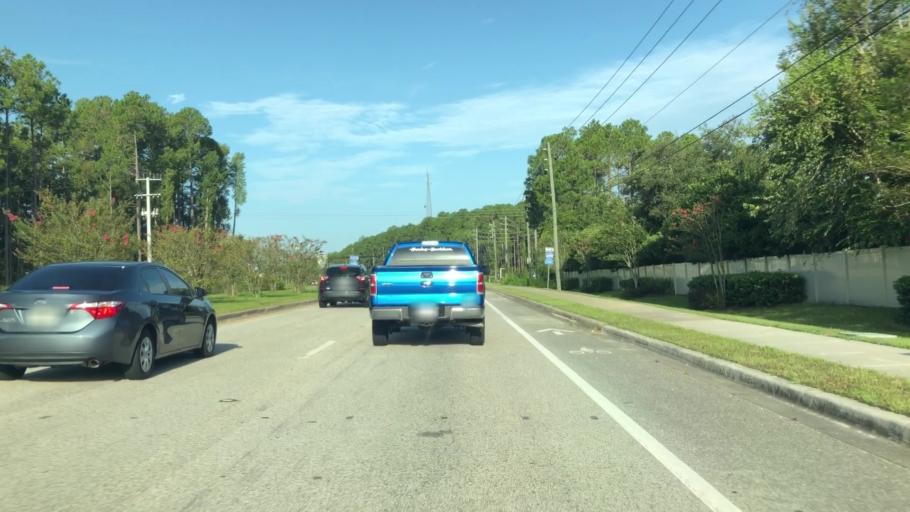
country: US
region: Florida
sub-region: Saint Johns County
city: Fruit Cove
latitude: 30.0600
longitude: -81.5283
